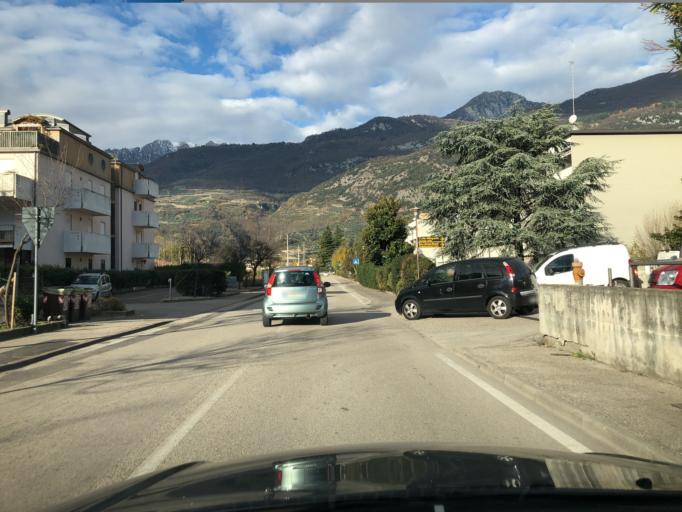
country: IT
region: Trentino-Alto Adige
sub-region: Provincia di Trento
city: Arco
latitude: 45.9134
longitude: 10.8756
